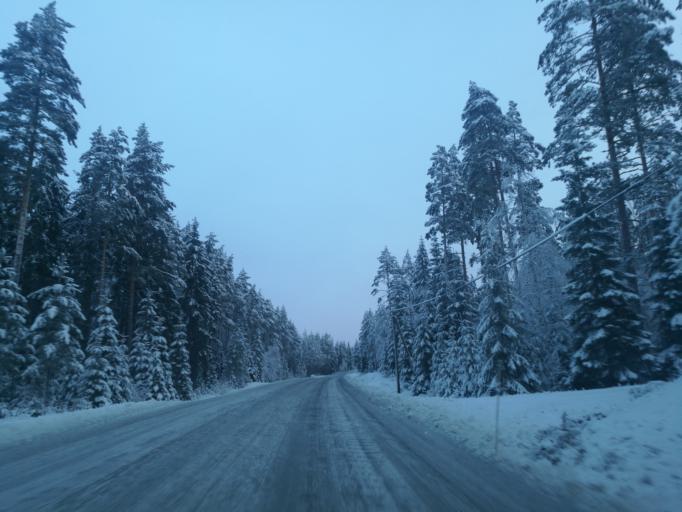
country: NO
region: Hedmark
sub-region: Grue
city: Kirkenaer
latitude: 60.3263
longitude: 12.2833
